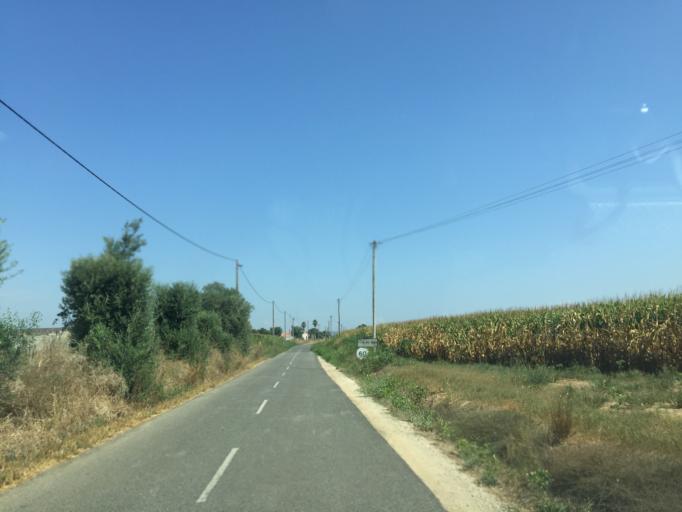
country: PT
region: Santarem
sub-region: Golega
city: Golega
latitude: 39.4071
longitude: -8.4715
